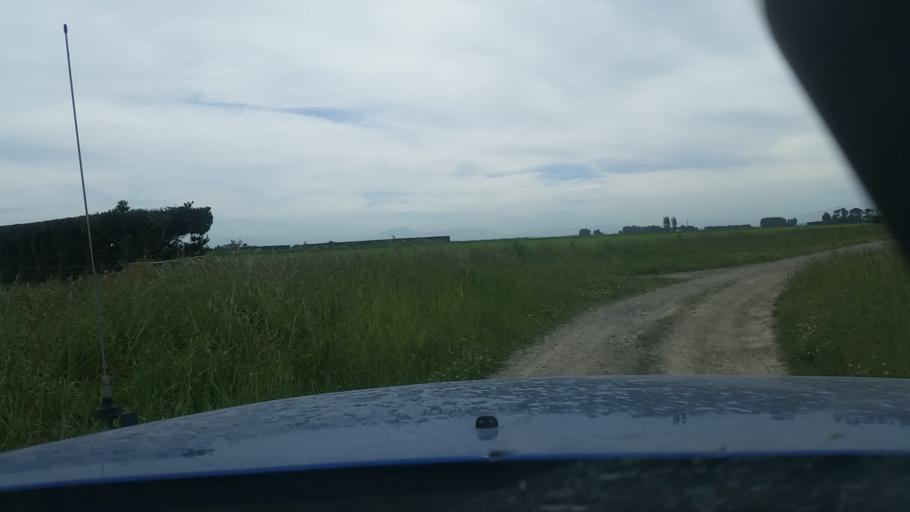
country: NZ
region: Canterbury
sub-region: Ashburton District
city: Tinwald
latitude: -44.0684
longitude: 171.7572
